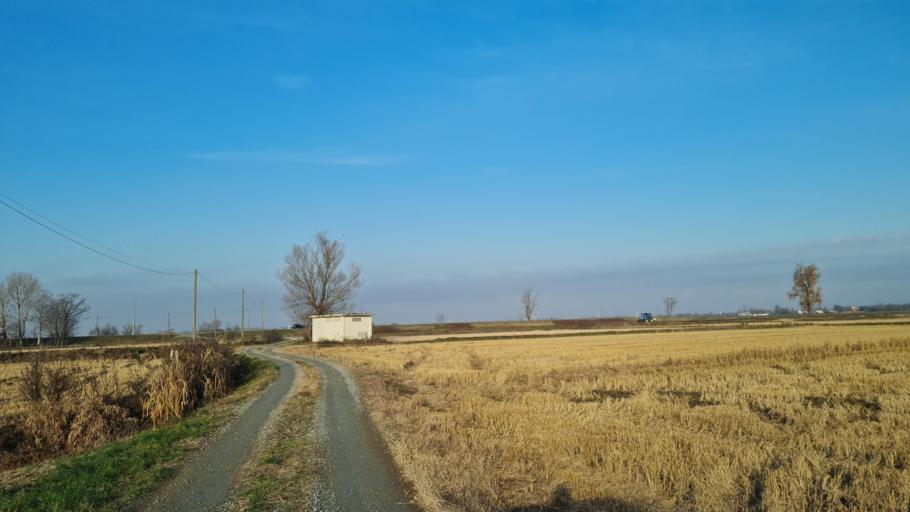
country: IT
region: Piedmont
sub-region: Provincia di Vercelli
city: Albano Vercellese
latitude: 45.4370
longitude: 8.3852
